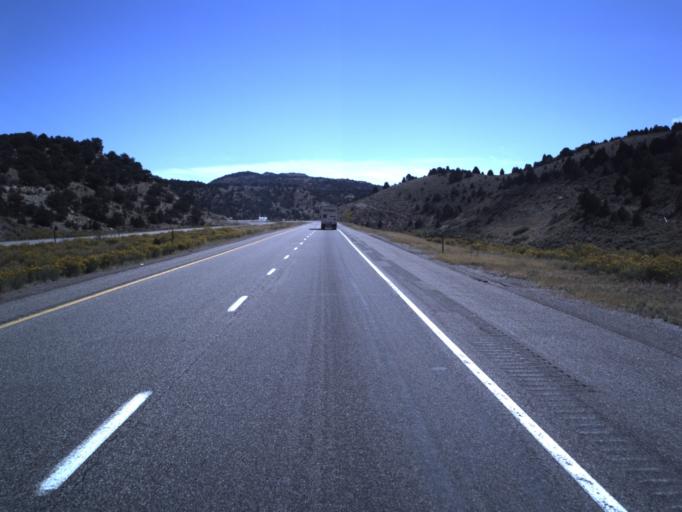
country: US
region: Utah
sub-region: Sevier County
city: Salina
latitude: 38.8043
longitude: -111.5268
